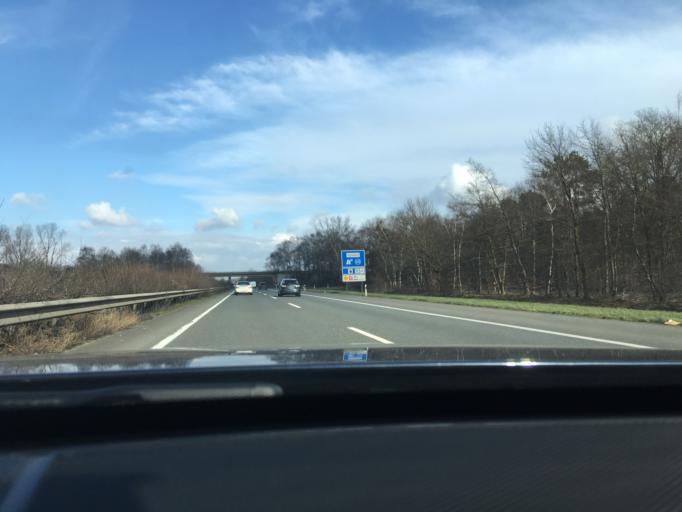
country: DE
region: Lower Saxony
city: Dinklage
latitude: 52.6364
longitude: 8.1479
